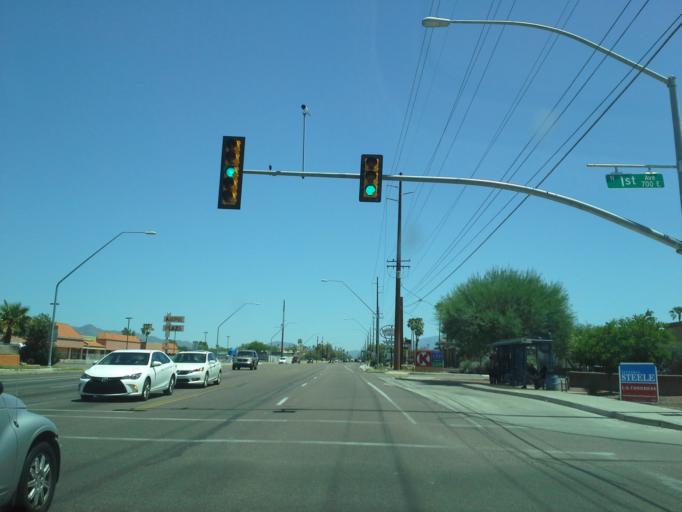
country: US
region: Arizona
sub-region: Pima County
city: Catalina Foothills
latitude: 32.2647
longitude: -110.9611
